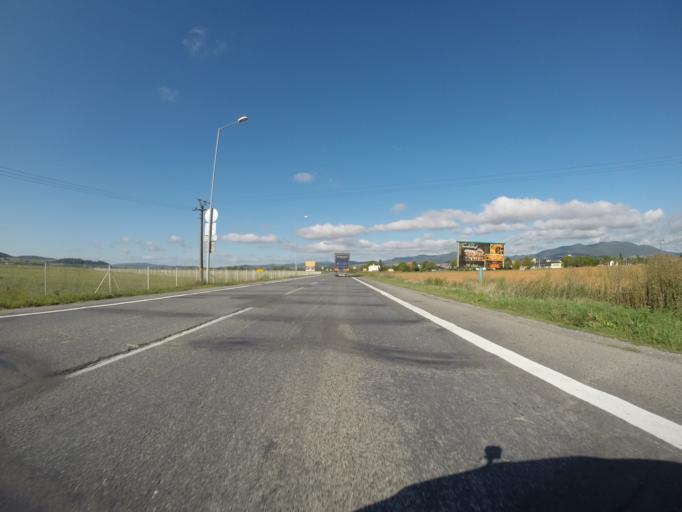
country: SK
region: Trenciansky
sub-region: Okres Trencin
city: Trencin
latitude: 48.8487
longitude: 17.9882
